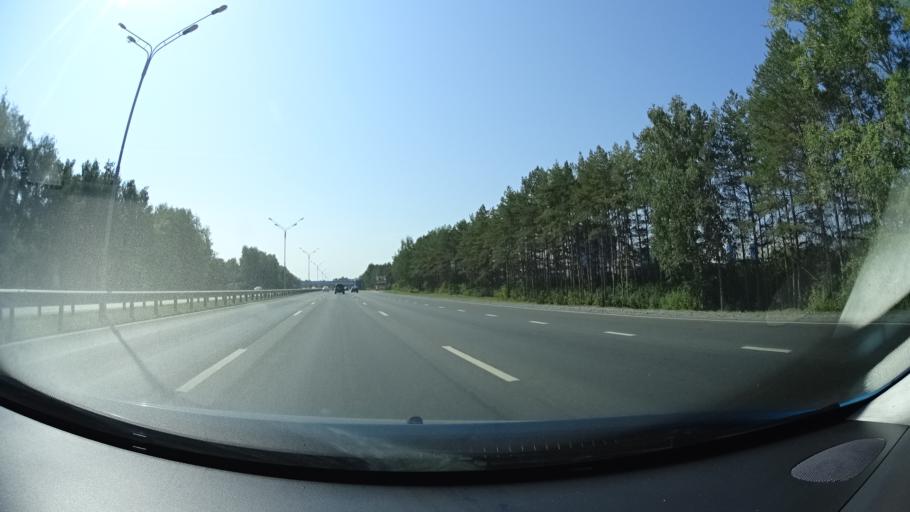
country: RU
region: Bashkortostan
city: Ufa
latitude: 54.5913
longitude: 55.9124
